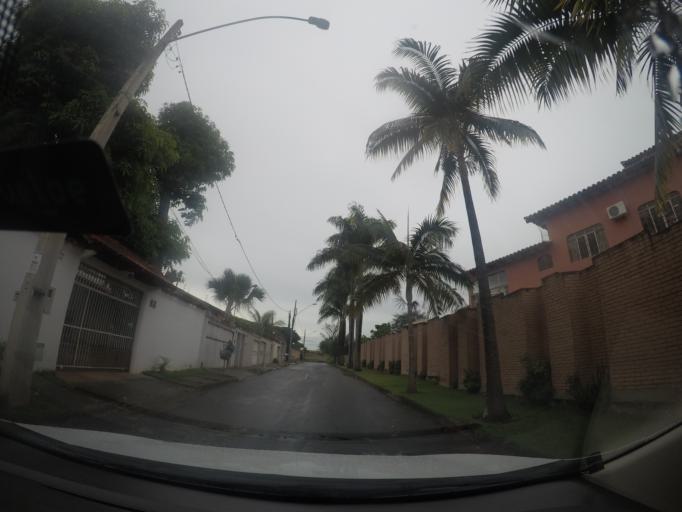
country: BR
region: Goias
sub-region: Goiania
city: Goiania
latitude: -16.6363
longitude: -49.2327
